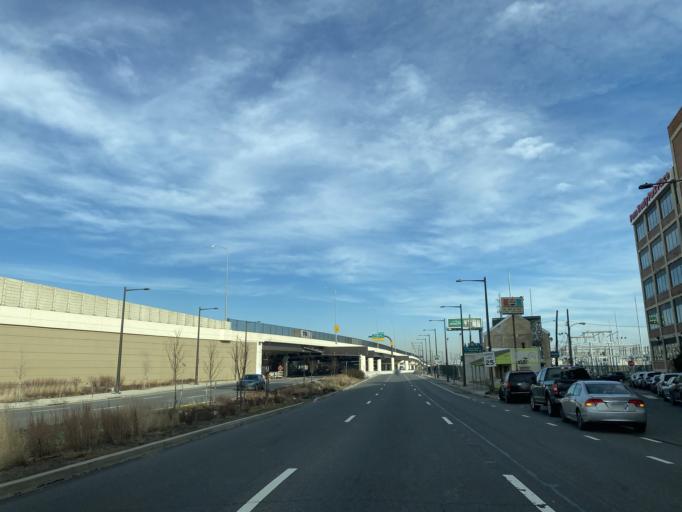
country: US
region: Pennsylvania
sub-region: Philadelphia County
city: Philadelphia
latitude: 39.9680
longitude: -75.1280
